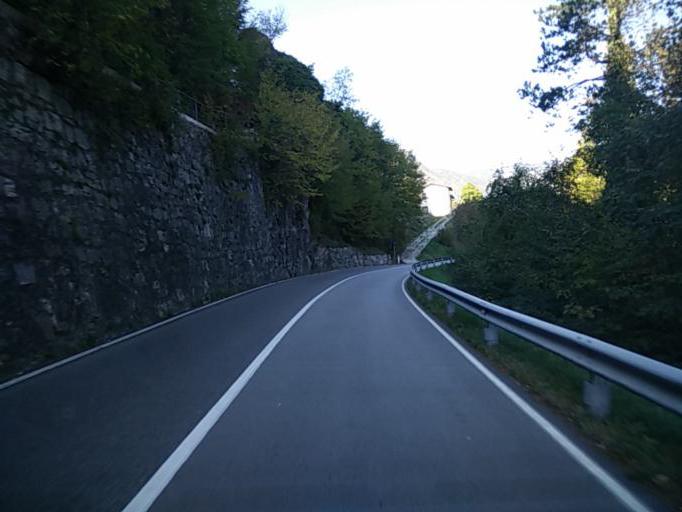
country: IT
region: Lombardy
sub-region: Provincia di Brescia
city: Anfo
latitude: 45.7777
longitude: 10.5032
